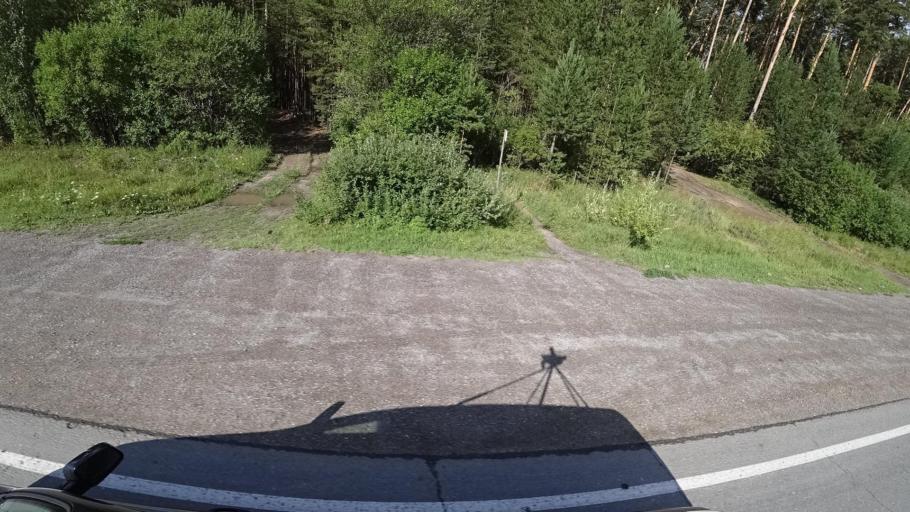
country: RU
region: Sverdlovsk
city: Kamyshlov
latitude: 56.8264
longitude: 62.7003
